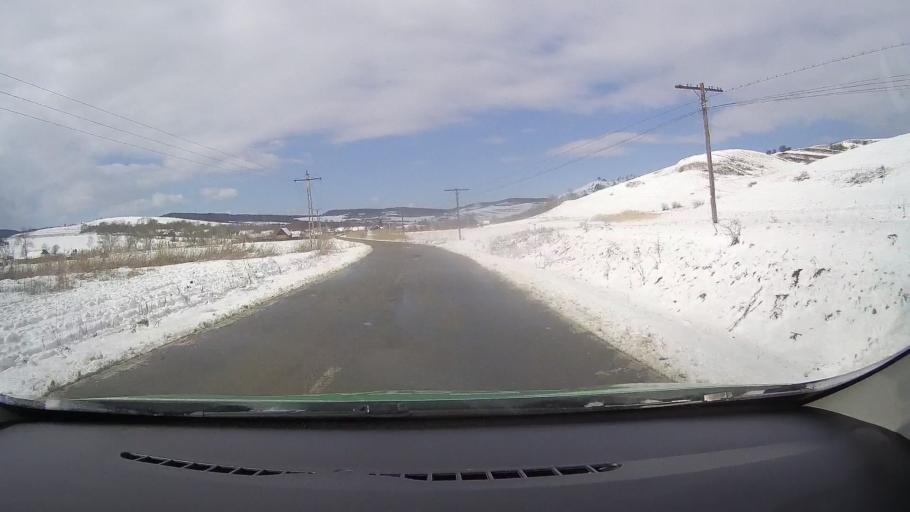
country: RO
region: Sibiu
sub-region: Comuna Altina
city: Altina
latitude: 45.9796
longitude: 24.4620
